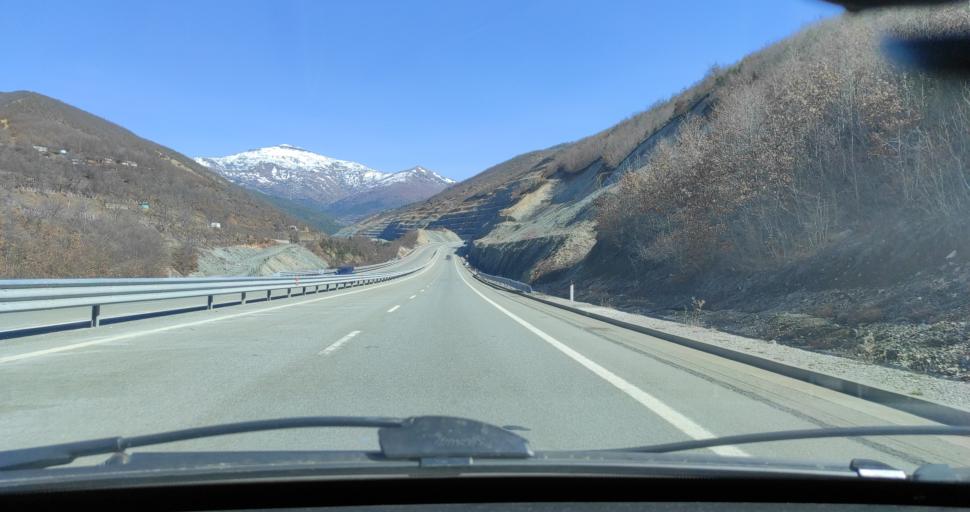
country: AL
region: Lezhe
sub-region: Rrethi i Lezhes
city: Shengjin
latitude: 41.9782
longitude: 20.1949
